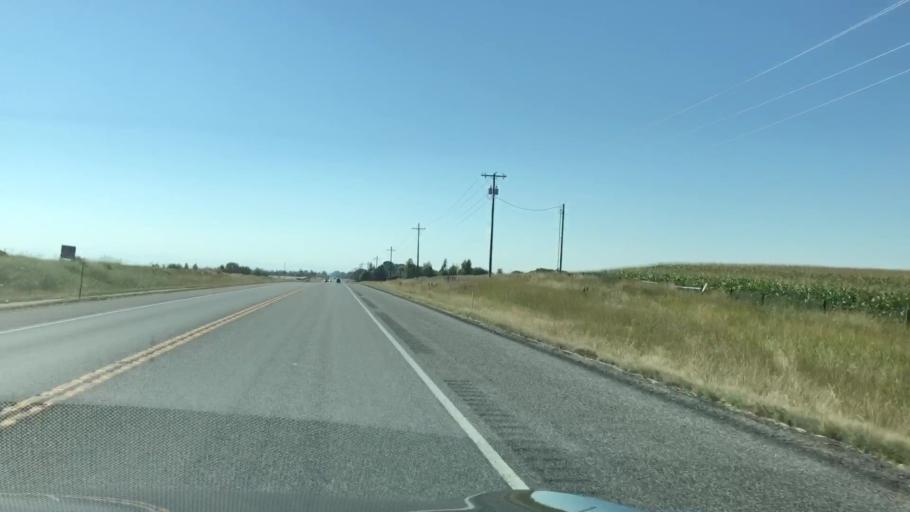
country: US
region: Montana
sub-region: Gallatin County
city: Belgrade
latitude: 45.7290
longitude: -111.1072
